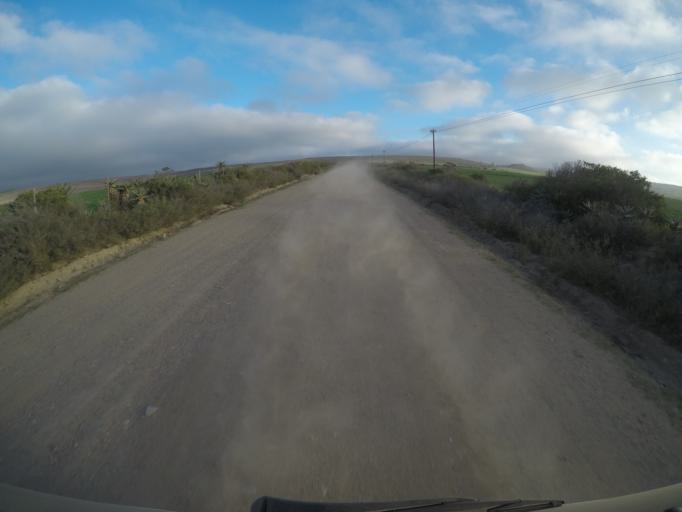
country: ZA
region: Western Cape
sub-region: Eden District Municipality
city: Mossel Bay
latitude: -34.1199
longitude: 22.0534
